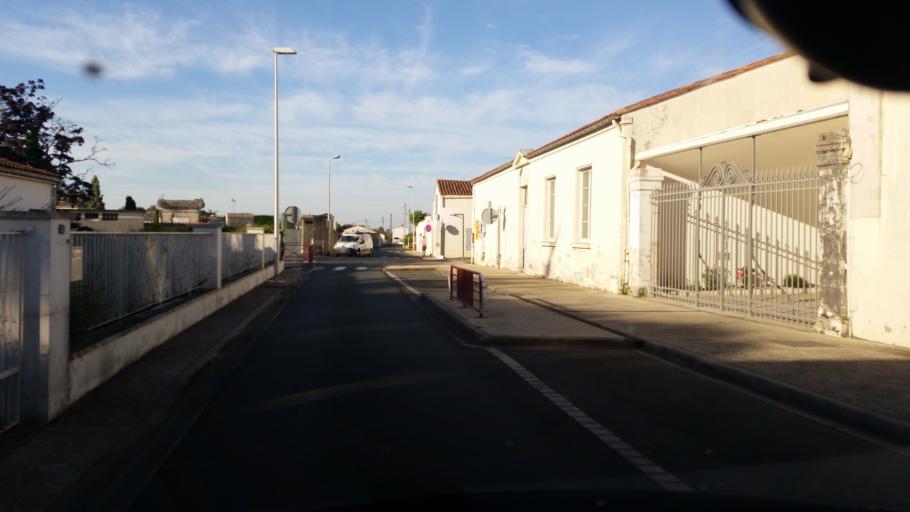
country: FR
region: Poitou-Charentes
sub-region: Departement de la Charente-Maritime
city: Marans
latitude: 46.3066
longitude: -0.9929
